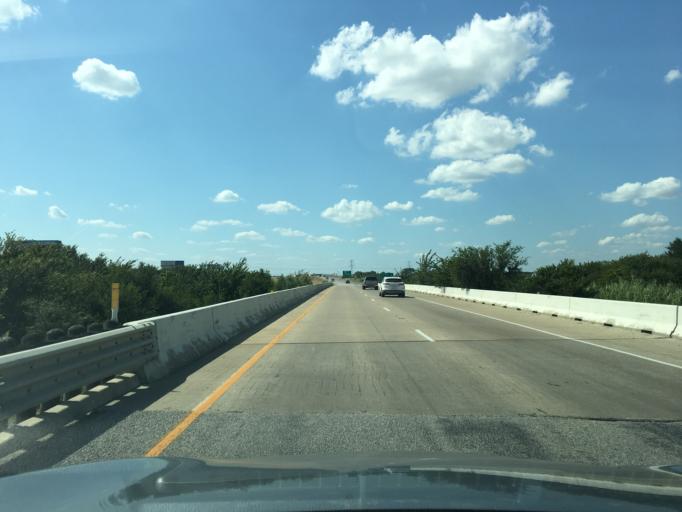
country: US
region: Texas
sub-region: Ellis County
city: Midlothian
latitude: 32.5128
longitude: -97.0669
